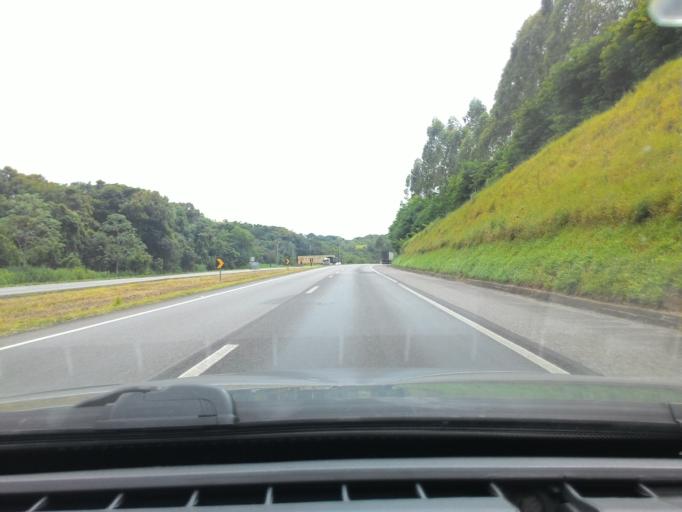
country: BR
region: Sao Paulo
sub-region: Registro
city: Registro
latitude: -24.5709
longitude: -47.8802
